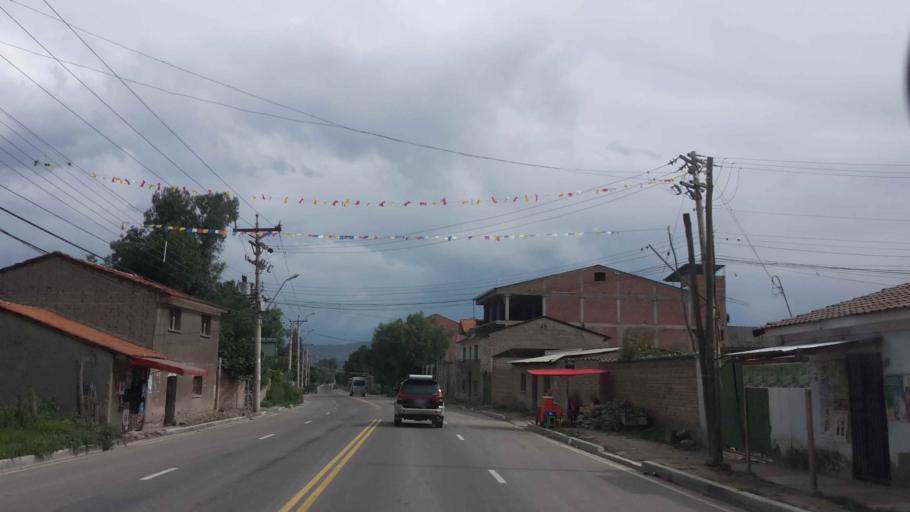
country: BO
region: Cochabamba
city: Cochabamba
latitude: -17.3684
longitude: -66.2527
